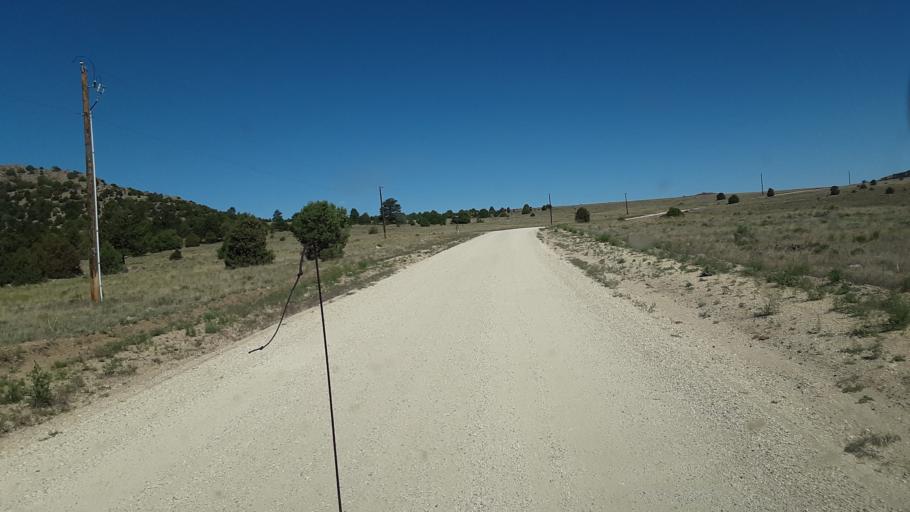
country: US
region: Colorado
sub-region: Custer County
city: Westcliffe
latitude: 38.2202
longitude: -105.4558
